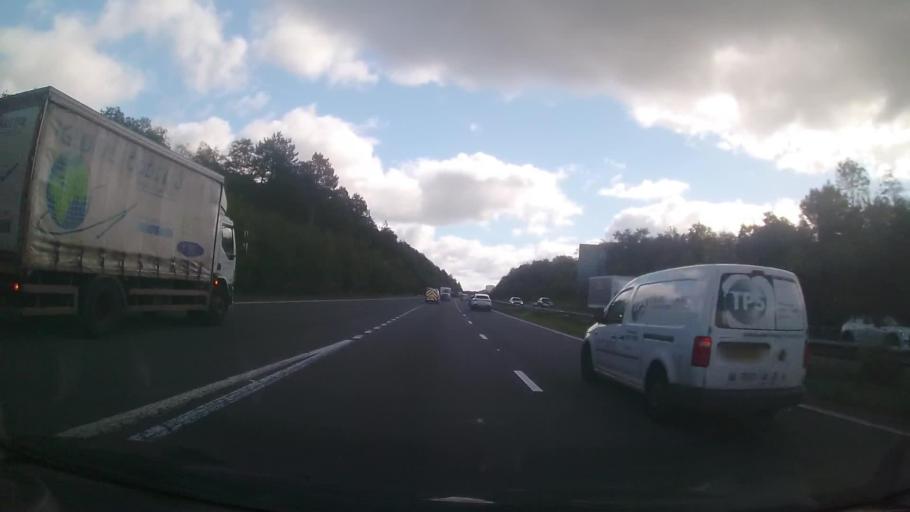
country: GB
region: Wales
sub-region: City and County of Swansea
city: Pontlliw
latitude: 51.6761
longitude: -3.9875
